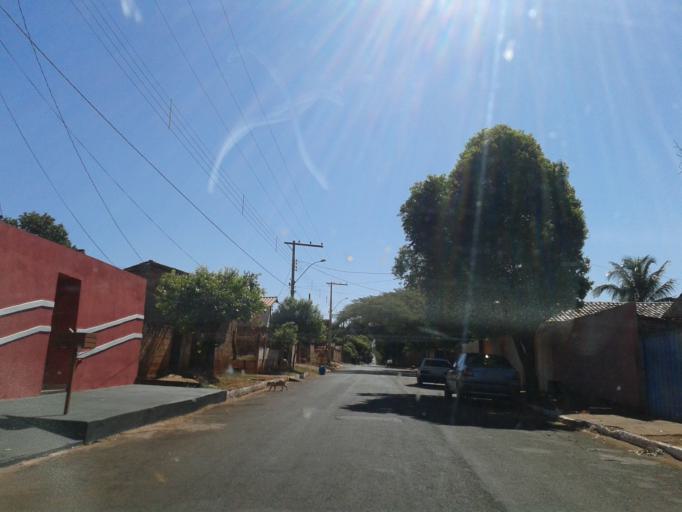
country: BR
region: Minas Gerais
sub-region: Santa Vitoria
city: Santa Vitoria
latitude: -18.8345
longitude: -50.1326
